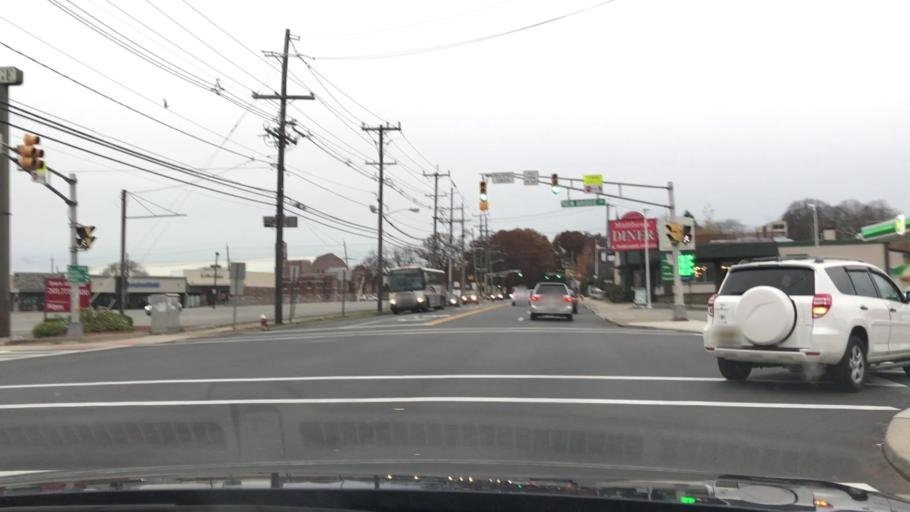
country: US
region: New Jersey
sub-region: Bergen County
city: Bergenfield
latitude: 40.9140
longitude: -73.9975
